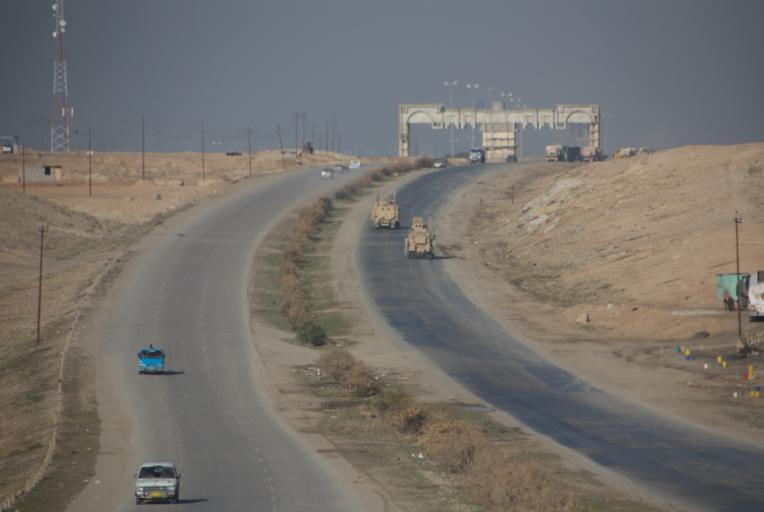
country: IQ
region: Ninawa
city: Al Mawsil al Jadidah
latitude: 36.2406
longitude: 43.1061
